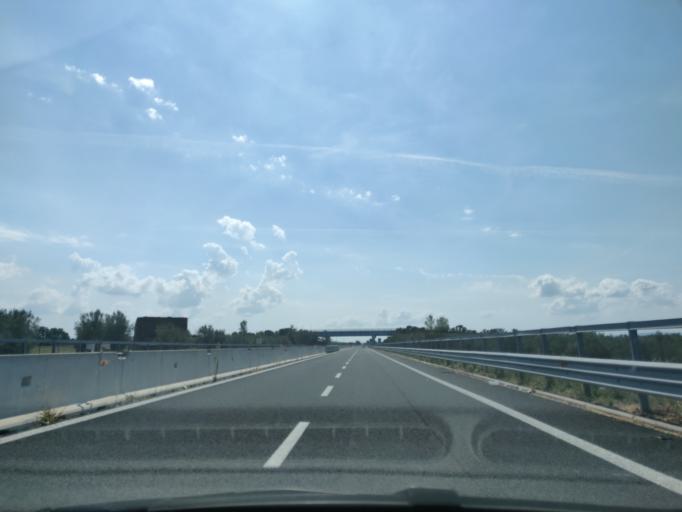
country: IT
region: Latium
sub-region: Provincia di Viterbo
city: Blera
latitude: 42.3184
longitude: 11.9909
